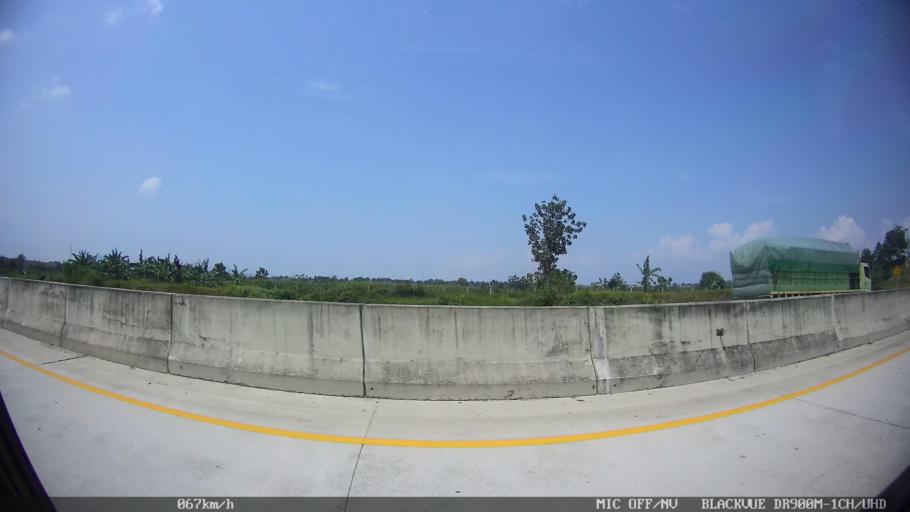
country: ID
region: Lampung
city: Kedaton
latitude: -5.3407
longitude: 105.3122
